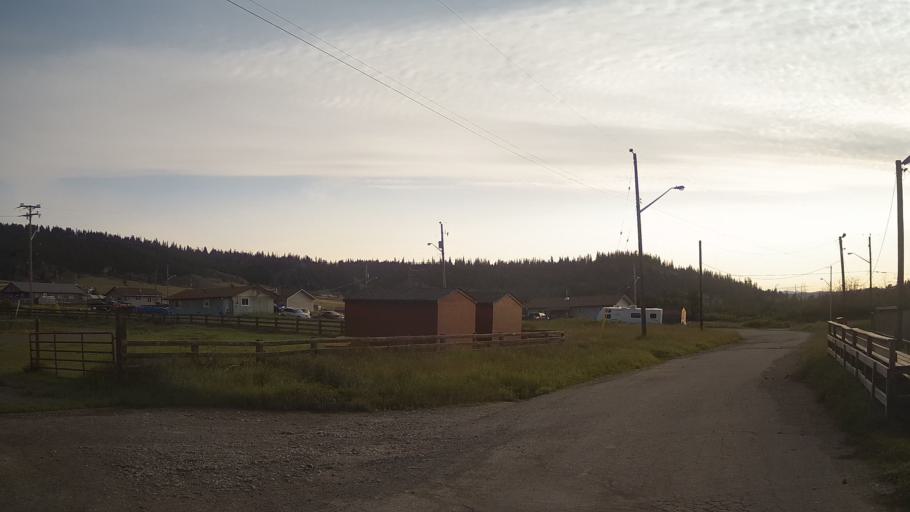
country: CA
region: British Columbia
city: Hanceville
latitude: 52.1361
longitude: -123.9512
